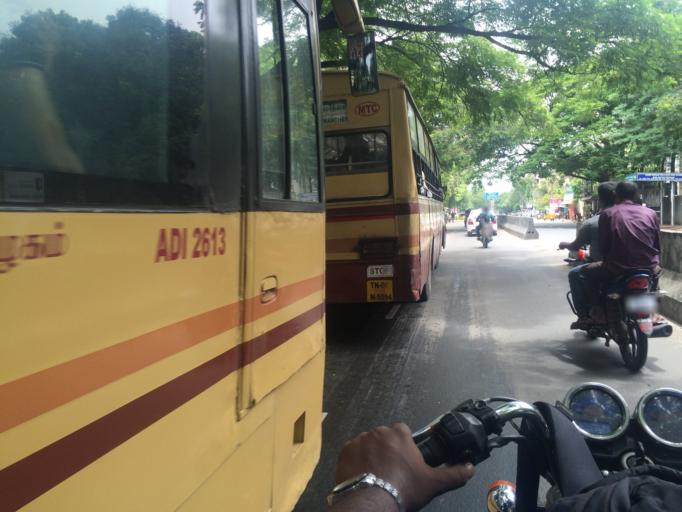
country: IN
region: Tamil Nadu
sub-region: Kancheepuram
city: Alandur
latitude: 12.9904
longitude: 80.2204
